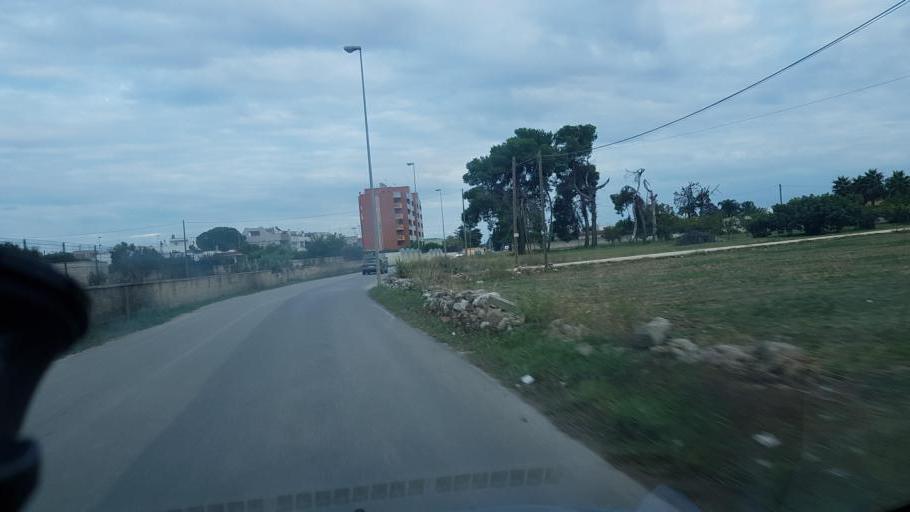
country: IT
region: Apulia
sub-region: Provincia di Brindisi
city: Latiano
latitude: 40.5481
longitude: 17.7251
